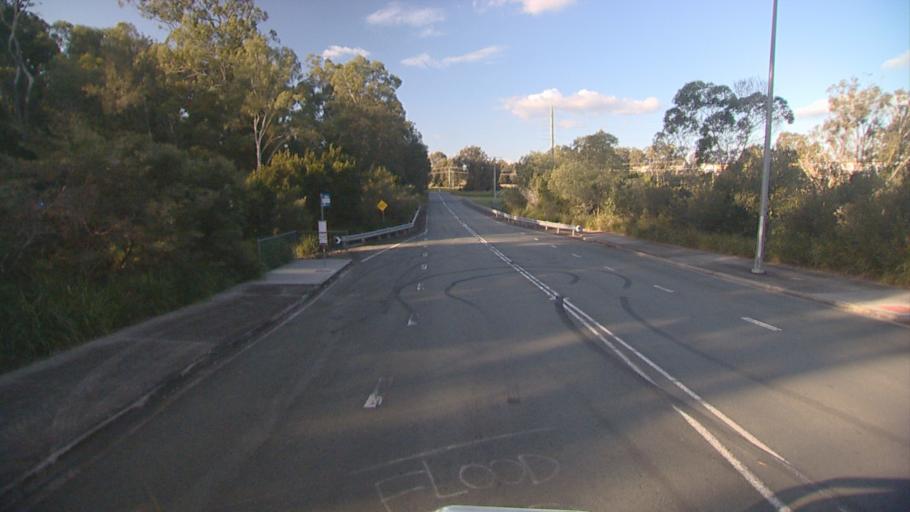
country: AU
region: Queensland
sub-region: Logan
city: Beenleigh
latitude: -27.7120
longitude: 153.1794
